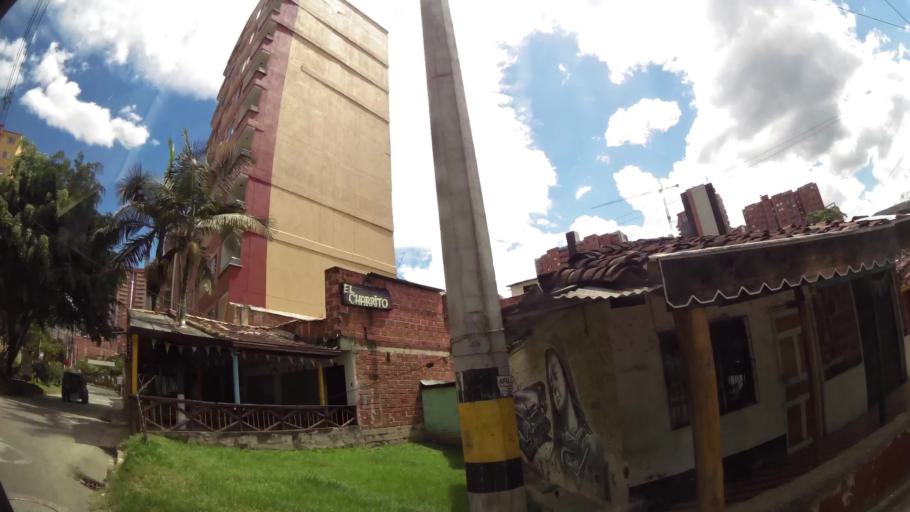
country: CO
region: Antioquia
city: Sabaneta
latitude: 6.1453
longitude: -75.6160
